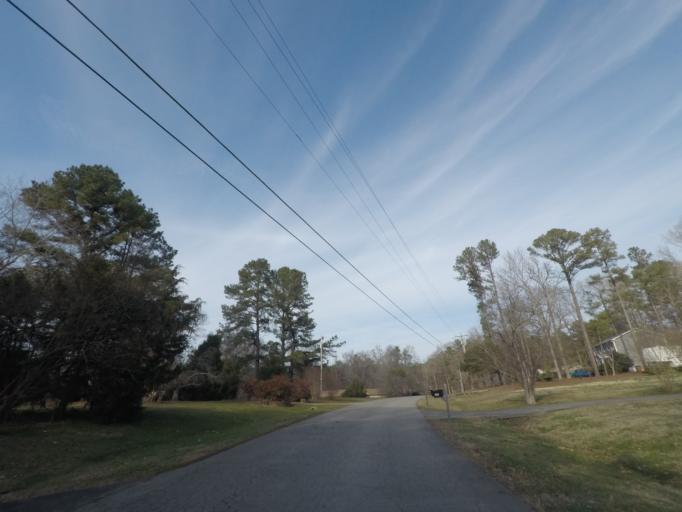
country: US
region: North Carolina
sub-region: Durham County
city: Durham
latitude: 36.0769
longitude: -78.9666
